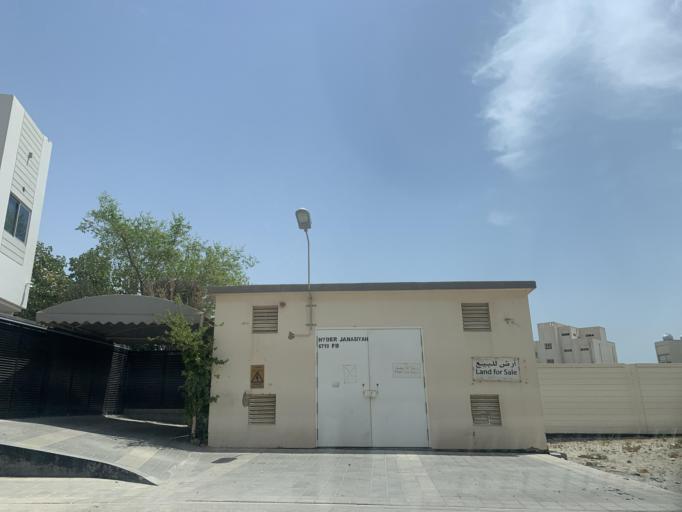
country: BH
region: Northern
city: Madinat `Isa
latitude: 26.1873
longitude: 50.4790
